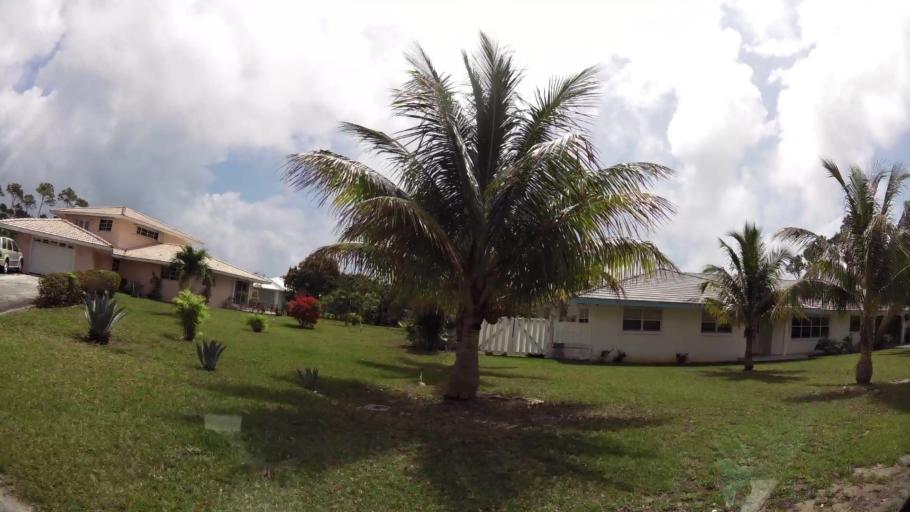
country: BS
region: Freeport
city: Lucaya
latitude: 26.5272
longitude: -78.6518
